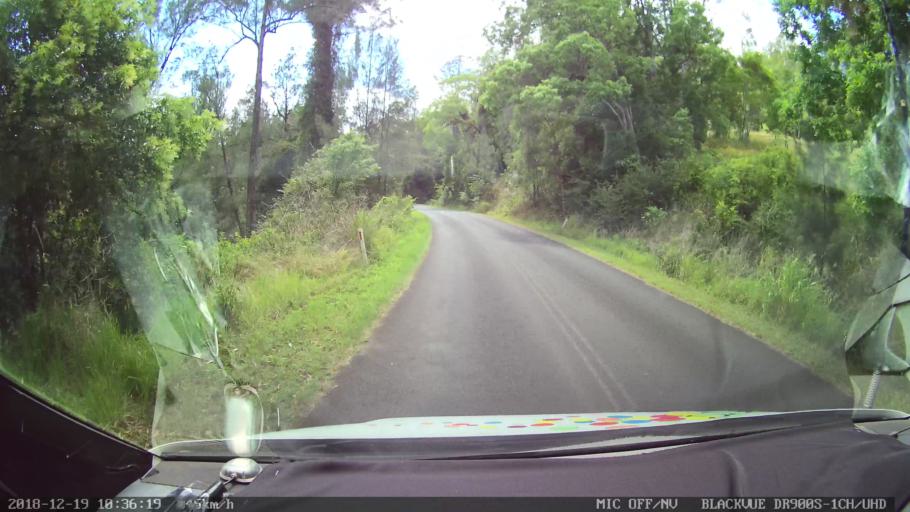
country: AU
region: New South Wales
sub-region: Lismore Municipality
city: Nimbin
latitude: -28.5743
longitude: 153.1433
